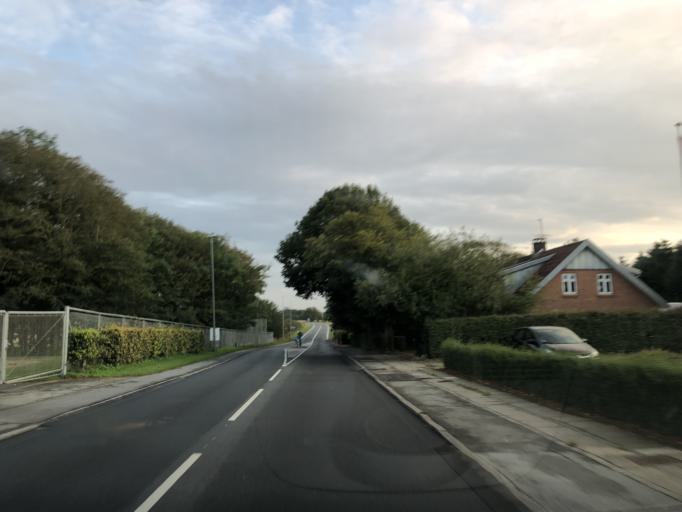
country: DK
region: Central Jutland
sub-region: Holstebro Kommune
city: Vinderup
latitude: 56.6100
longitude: 8.8793
